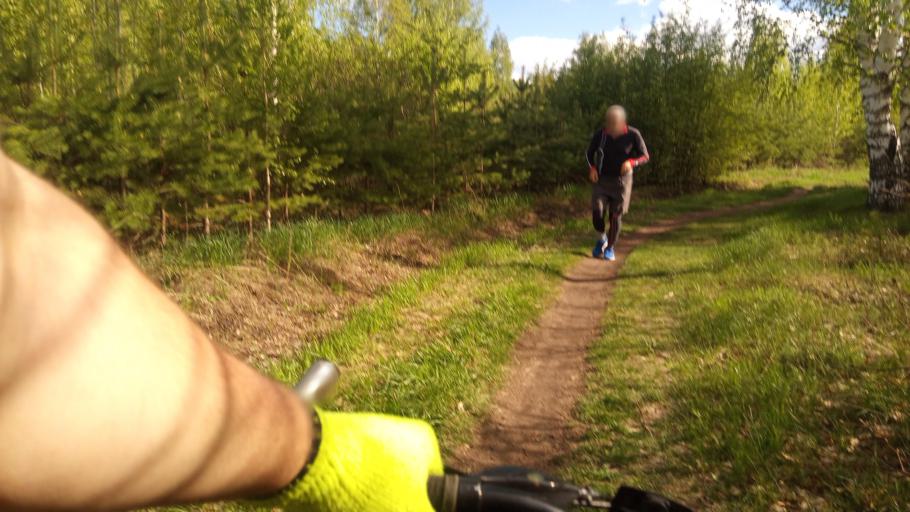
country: RU
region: Chelyabinsk
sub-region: Gorod Chelyabinsk
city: Chelyabinsk
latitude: 55.1655
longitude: 61.3160
